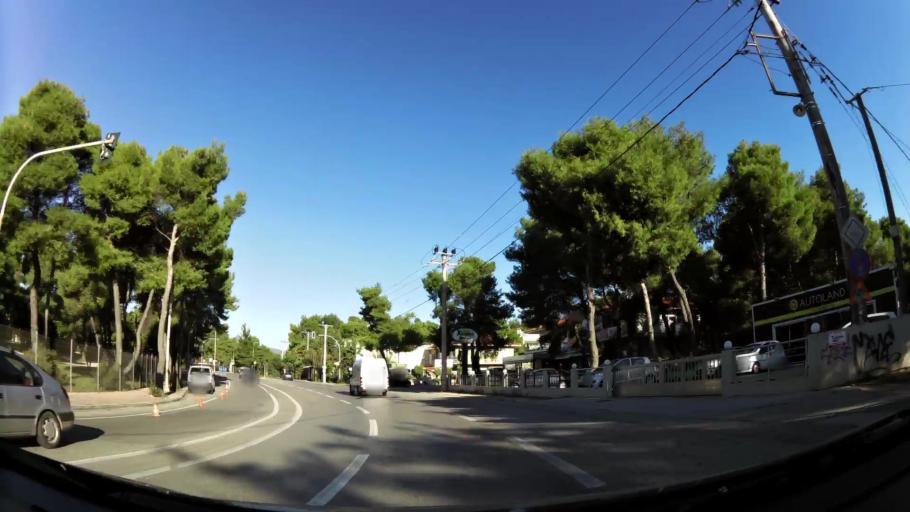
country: GR
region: Attica
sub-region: Nomarchia Anatolikis Attikis
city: Drosia
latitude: 38.1222
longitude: 23.8584
